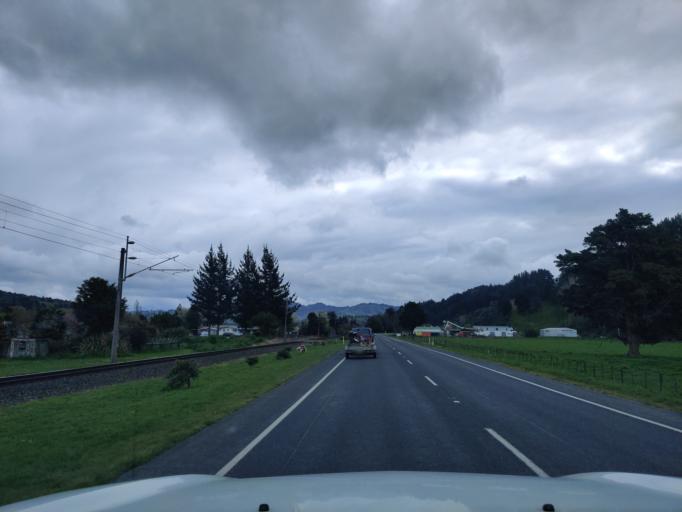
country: NZ
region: Waikato
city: Turangi
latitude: -38.8816
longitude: 175.2858
